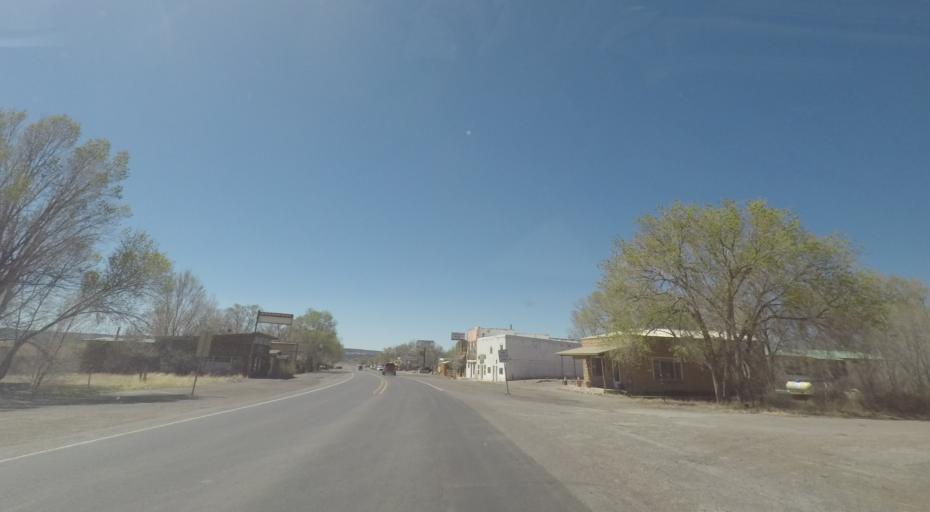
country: US
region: New Mexico
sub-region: Catron County
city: Reserve
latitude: 34.3426
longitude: -108.4945
